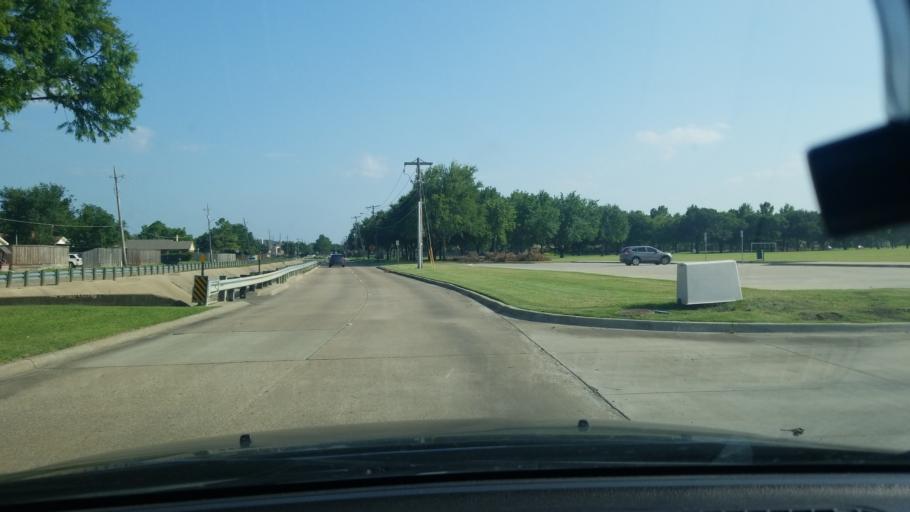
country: US
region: Texas
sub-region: Dallas County
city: Sunnyvale
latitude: 32.8194
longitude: -96.6073
